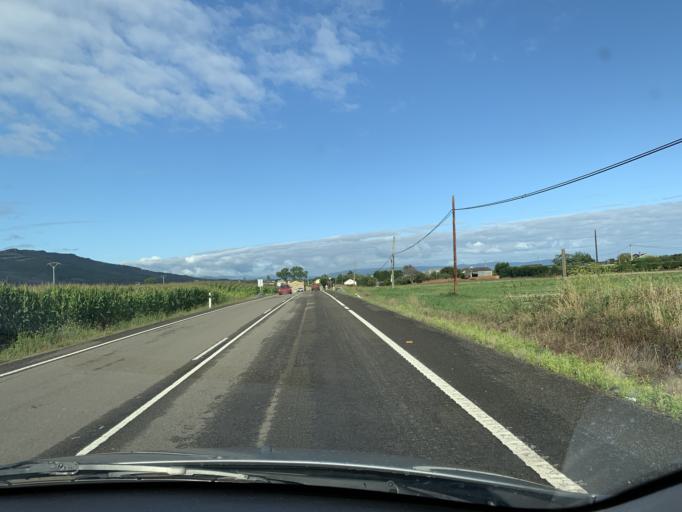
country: ES
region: Galicia
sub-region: Provincia de Lugo
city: Ribadeo
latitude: 43.5469
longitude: -7.1124
